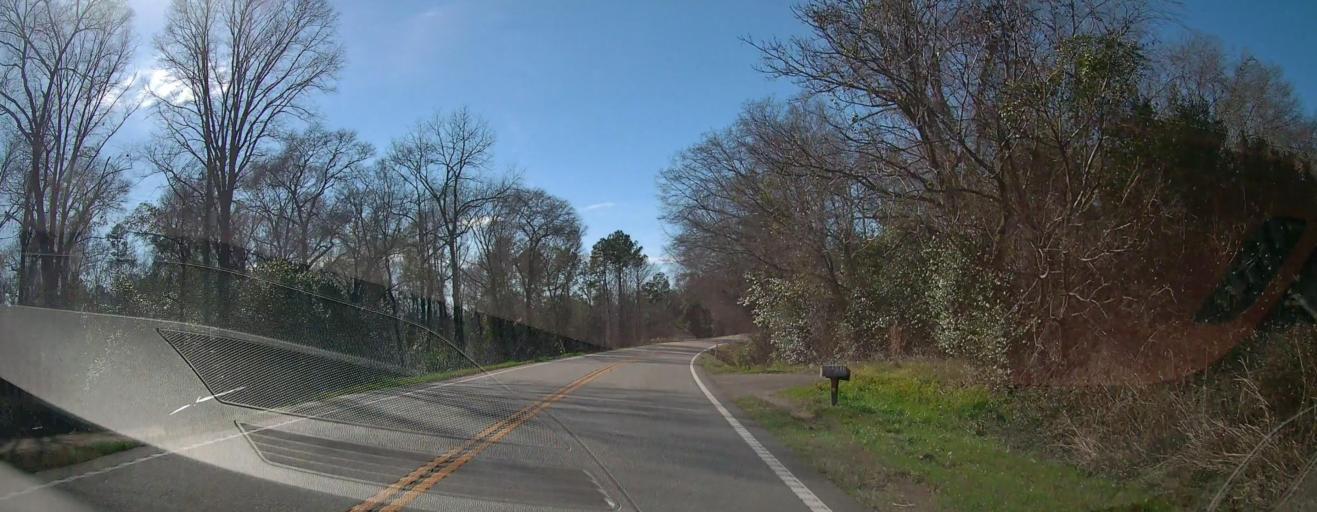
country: US
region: Georgia
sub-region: Macon County
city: Oglethorpe
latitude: 32.3516
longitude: -84.1688
